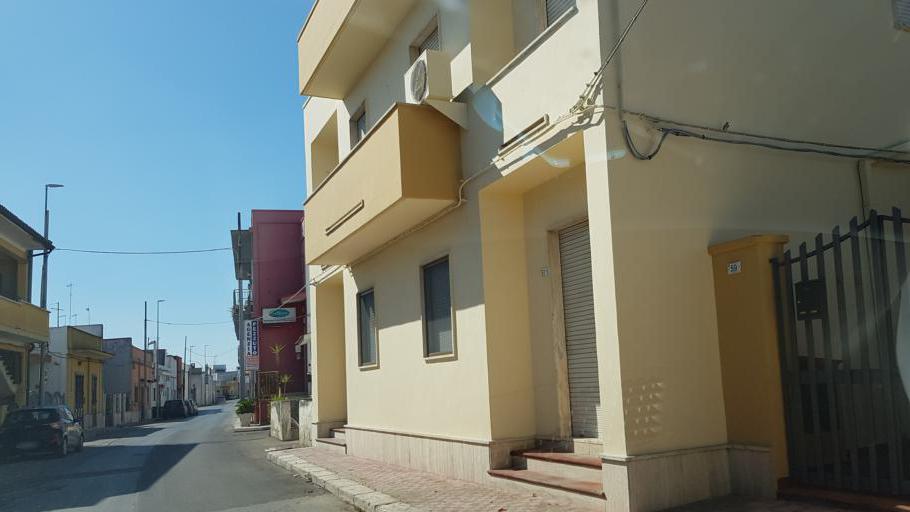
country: IT
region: Apulia
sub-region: Provincia di Brindisi
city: San Donaci
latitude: 40.4451
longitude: 17.9262
